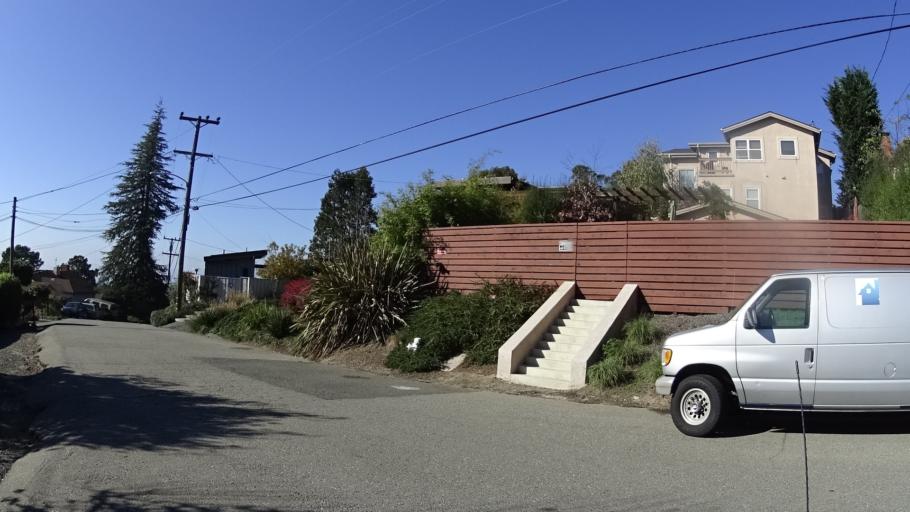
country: US
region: California
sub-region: Alameda County
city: Piedmont
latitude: 37.8307
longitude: -122.2070
